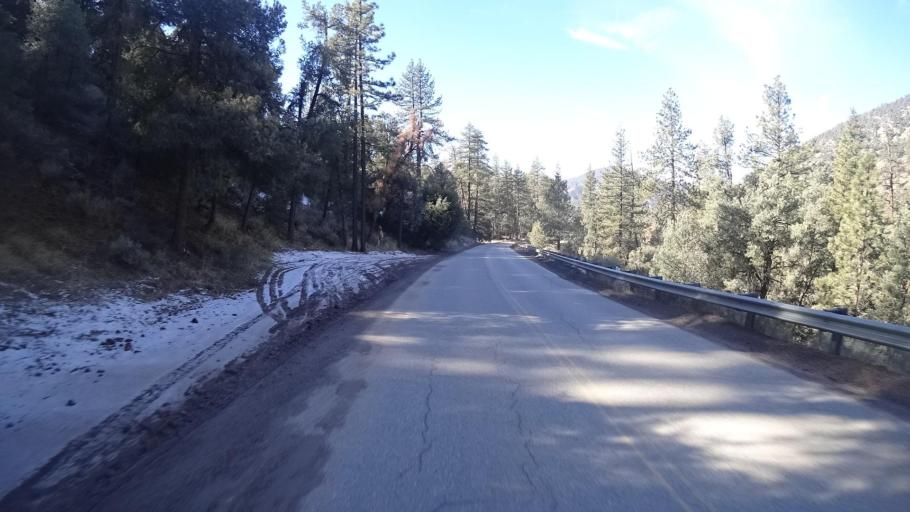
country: US
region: California
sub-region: Kern County
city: Pine Mountain Club
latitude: 34.8498
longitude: -119.1049
